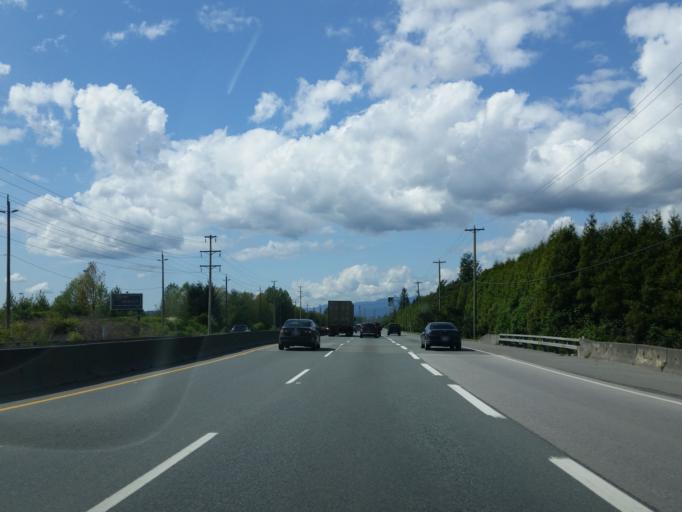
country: CA
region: British Columbia
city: Pitt Meadows
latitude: 49.2379
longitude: -122.7068
